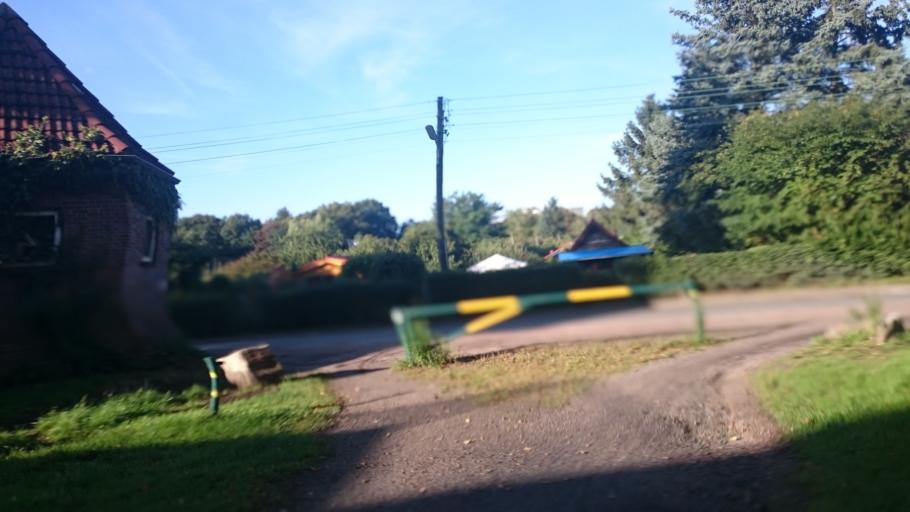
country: DE
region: Hamburg
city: Stellingen
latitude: 53.5726
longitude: 9.9096
